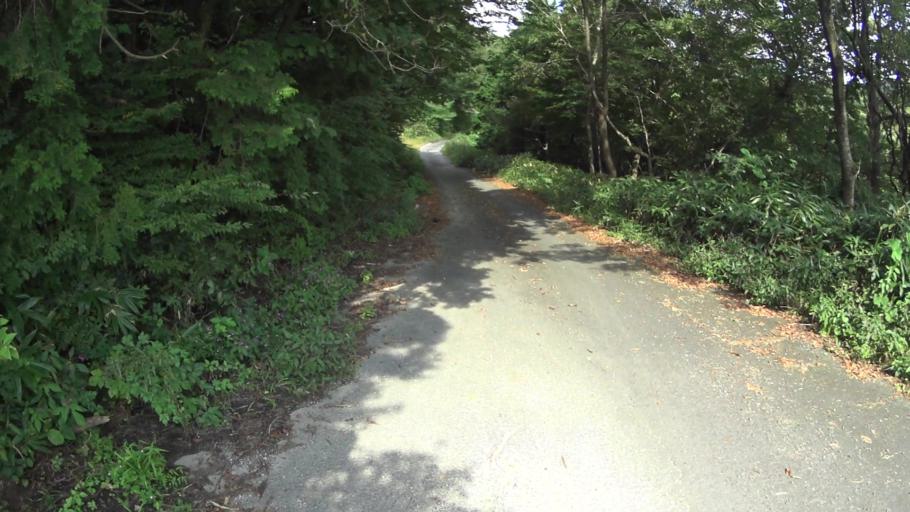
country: JP
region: Kyoto
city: Miyazu
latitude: 35.6392
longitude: 135.1820
